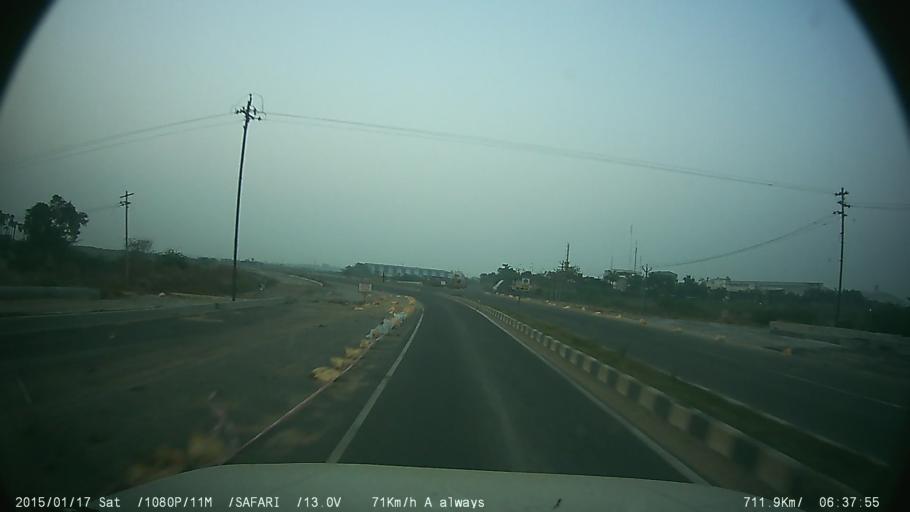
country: IN
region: Tamil Nadu
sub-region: Kancheepuram
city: Sriperumbudur
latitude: 12.9410
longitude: 79.9358
